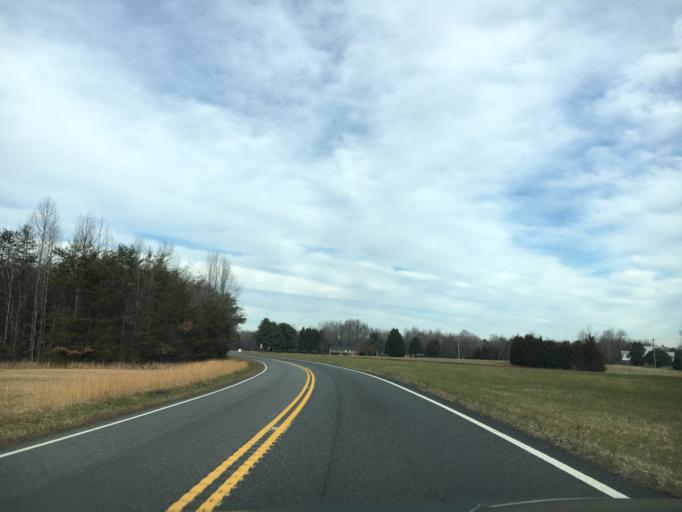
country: US
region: Virginia
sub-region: Goochland County
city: Goochland
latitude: 37.8045
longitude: -77.8617
